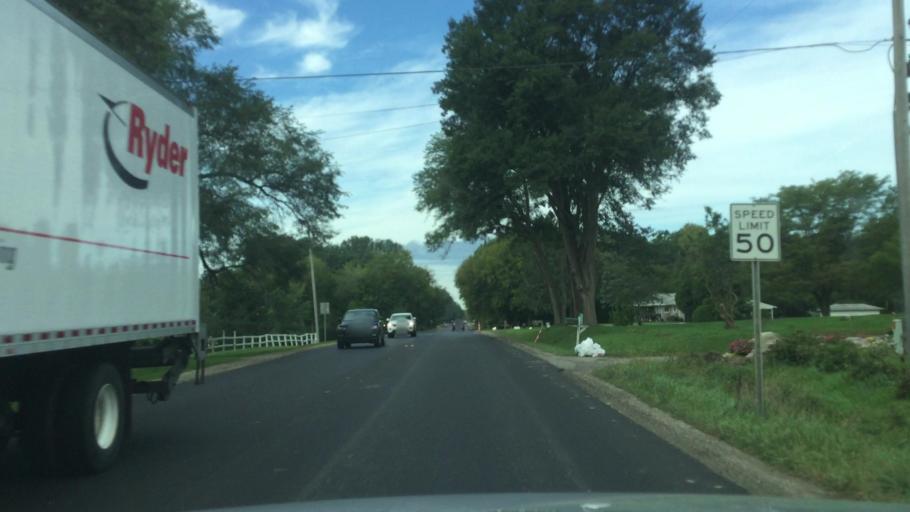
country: US
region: Michigan
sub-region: Oakland County
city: Holly
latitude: 42.8145
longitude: -83.5812
